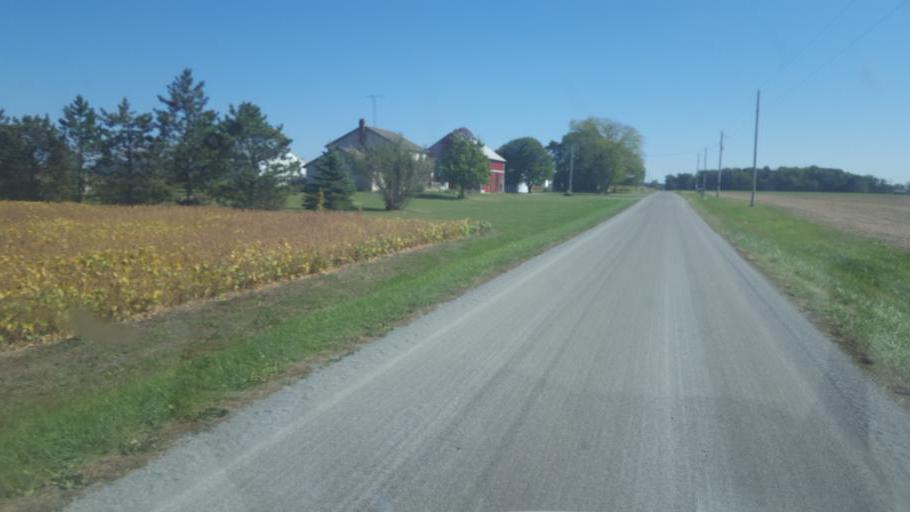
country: US
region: Ohio
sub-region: Wyandot County
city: Upper Sandusky
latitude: 40.8476
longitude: -83.2075
